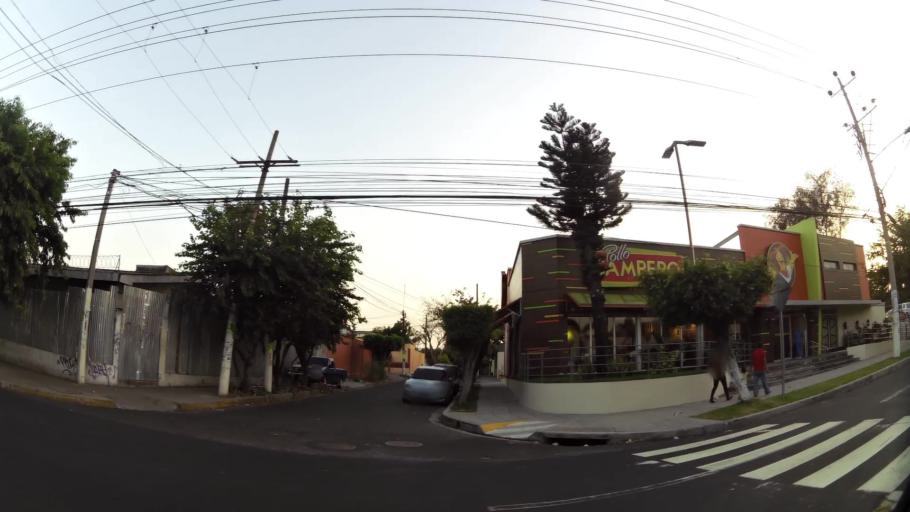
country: SV
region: San Salvador
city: Mejicanos
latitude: 13.7155
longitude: -89.2138
